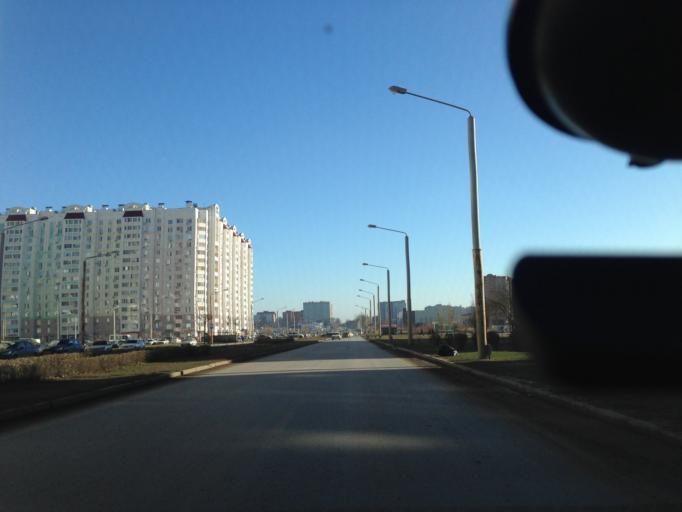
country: RU
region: Rostov
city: Kalinin
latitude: 47.2322
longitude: 39.5982
